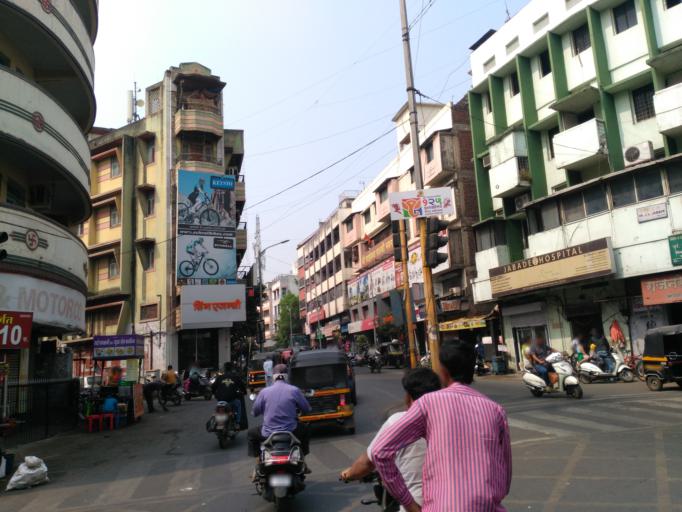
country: IN
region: Maharashtra
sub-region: Pune Division
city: Pune
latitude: 18.5187
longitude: 73.8595
